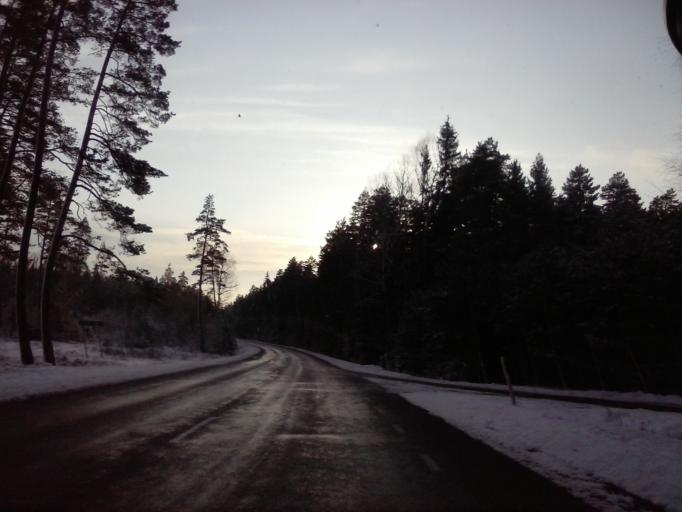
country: EE
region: Tartu
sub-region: UElenurme vald
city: Ulenurme
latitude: 58.3373
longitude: 26.8972
